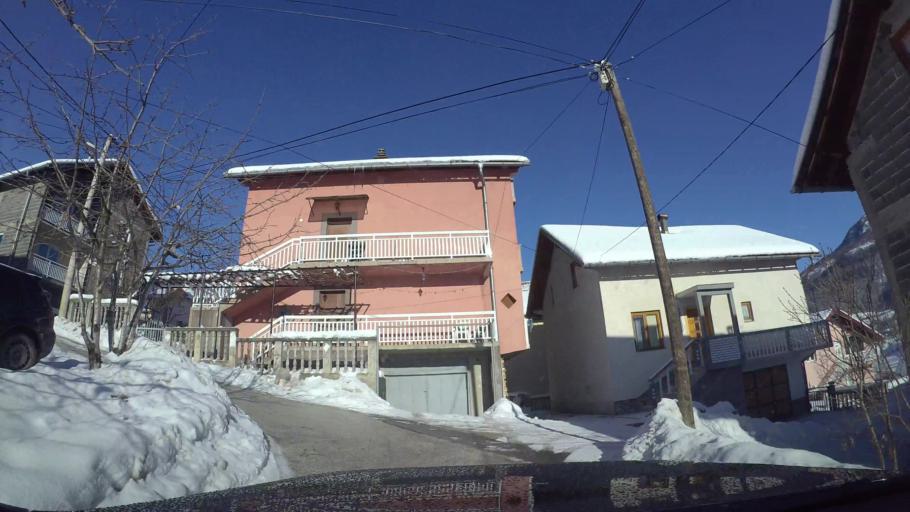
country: BA
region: Federation of Bosnia and Herzegovina
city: Kobilja Glava
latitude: 43.8923
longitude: 18.4093
